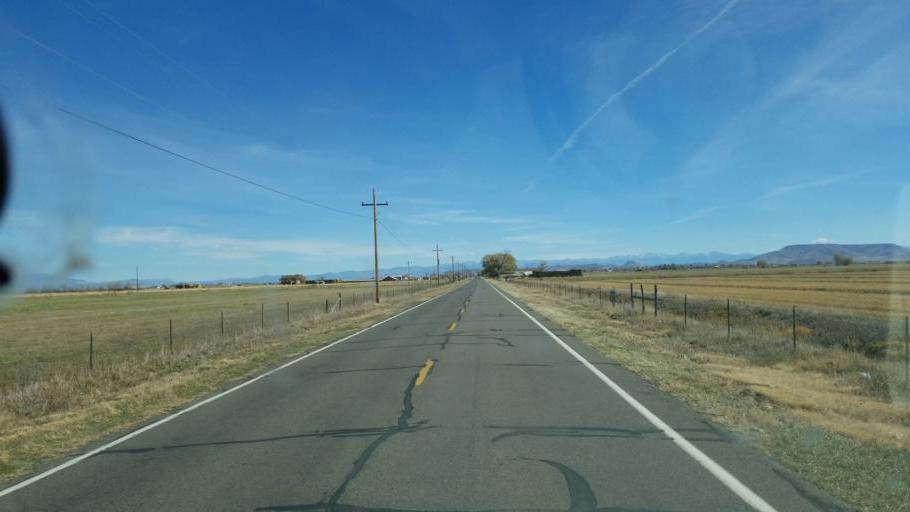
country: US
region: Colorado
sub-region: Conejos County
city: Conejos
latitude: 37.2835
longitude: -106.0044
